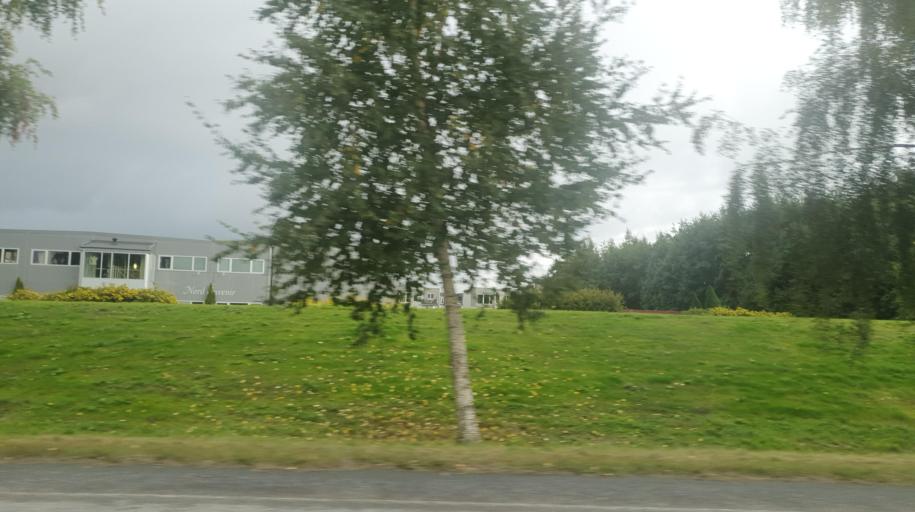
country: NO
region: Nord-Trondelag
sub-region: Verdal
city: Verdal
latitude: 63.7910
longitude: 11.4889
